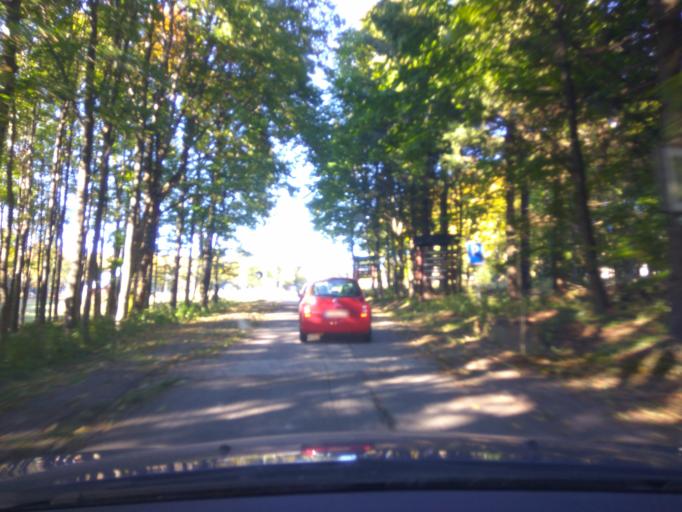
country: SK
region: Banskobystricky
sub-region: Okres Ziar nad Hronom
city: Kremnica
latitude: 48.7382
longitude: 18.9886
